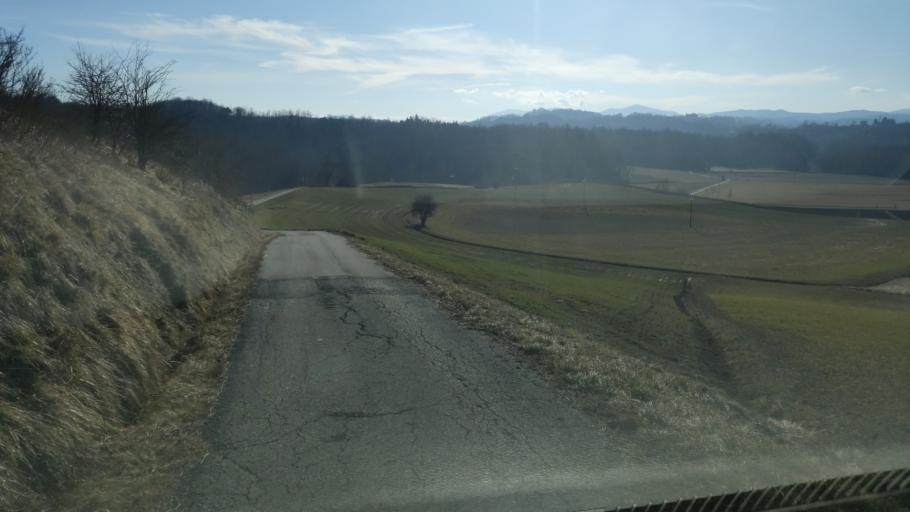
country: IT
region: Piedmont
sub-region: Provincia di Cuneo
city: Camerana
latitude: 44.4121
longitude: 8.1290
